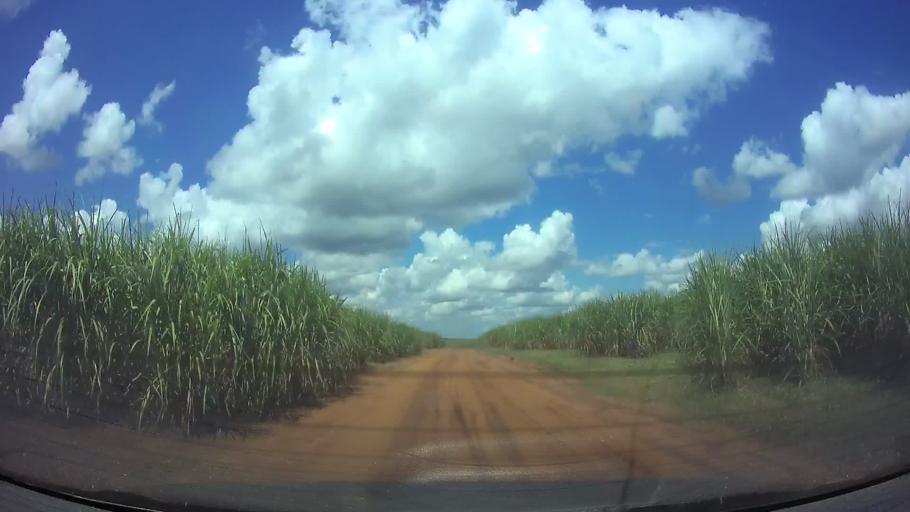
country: PY
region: Paraguari
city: La Colmena
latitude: -25.9644
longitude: -56.7618
